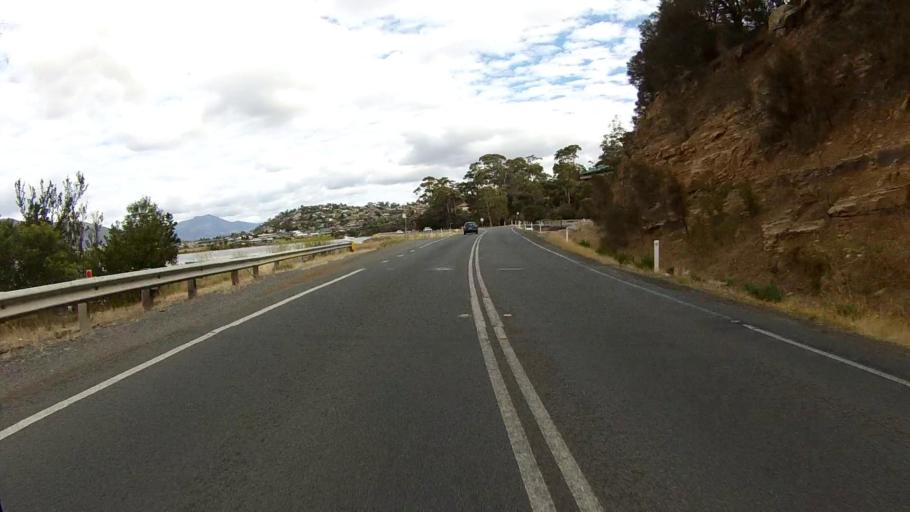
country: AU
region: Tasmania
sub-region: Brighton
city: Old Beach
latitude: -42.7843
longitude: 147.2882
